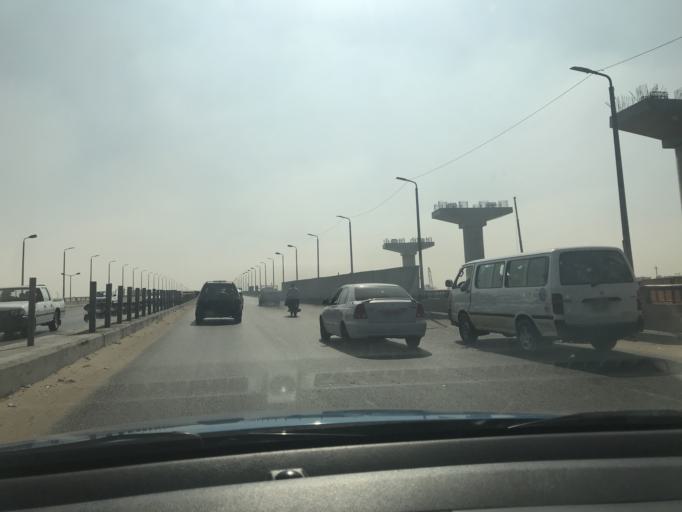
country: EG
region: Muhafazat al Qalyubiyah
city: Al Khankah
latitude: 30.1467
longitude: 31.4167
